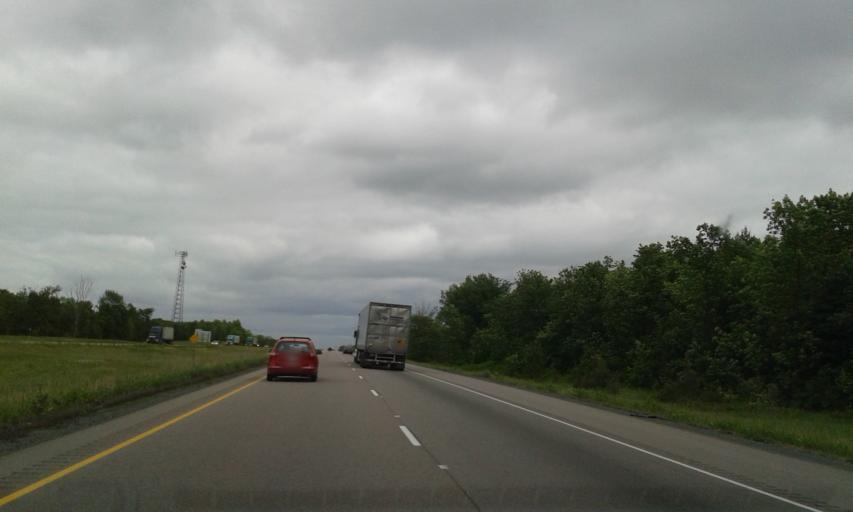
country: CA
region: Ontario
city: Skatepark
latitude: 44.2795
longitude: -76.7717
